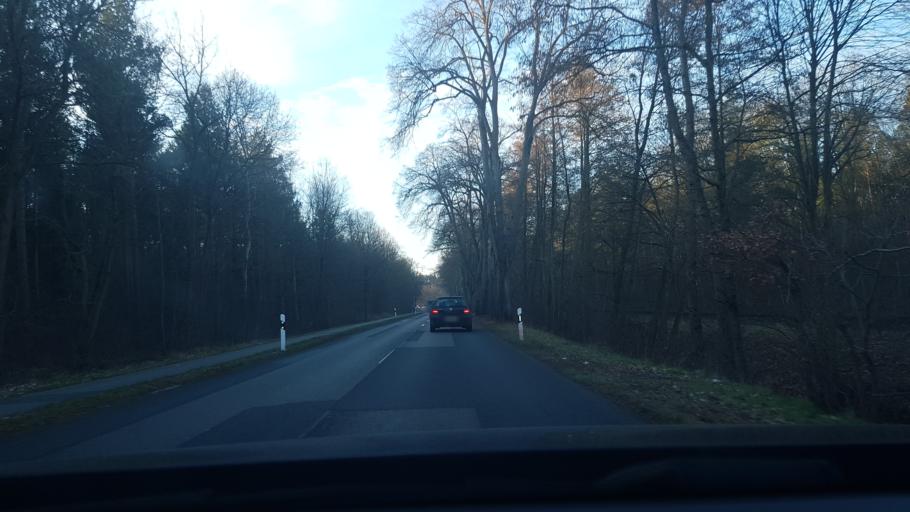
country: DE
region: Lower Saxony
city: Gifhorn
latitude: 52.5003
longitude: 10.5722
